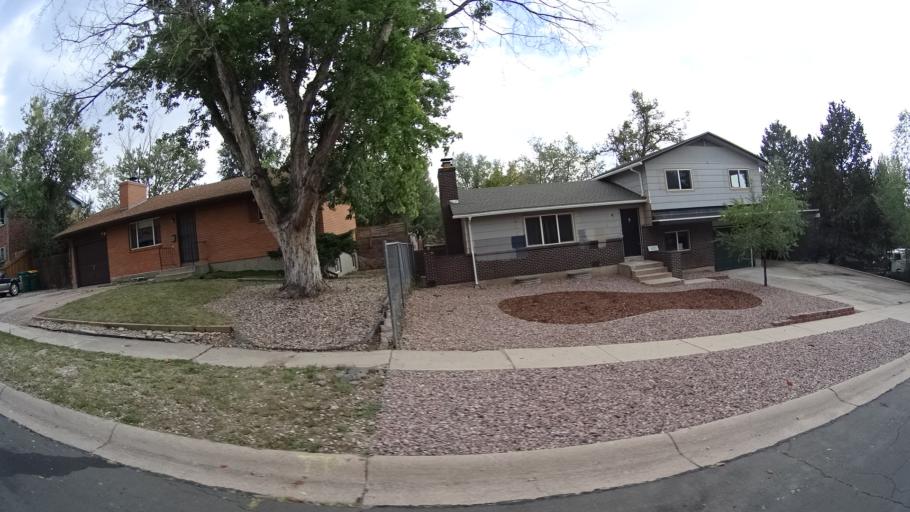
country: US
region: Colorado
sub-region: El Paso County
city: Colorado Springs
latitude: 38.8534
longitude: -104.7692
